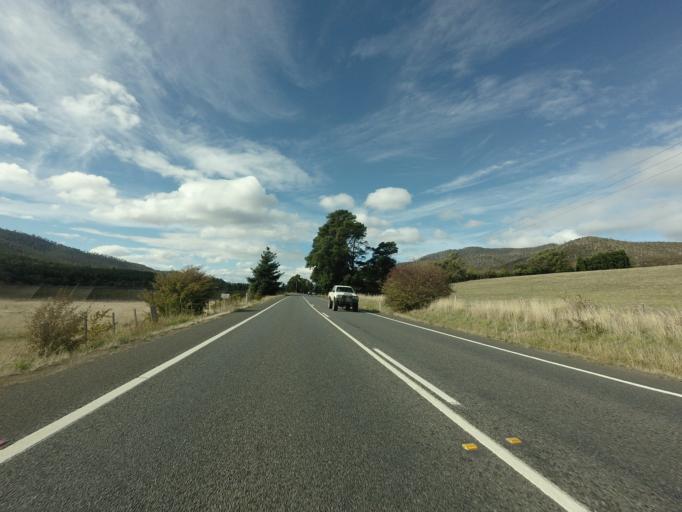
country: AU
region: Tasmania
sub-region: Derwent Valley
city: New Norfolk
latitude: -42.7743
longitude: 147.1203
